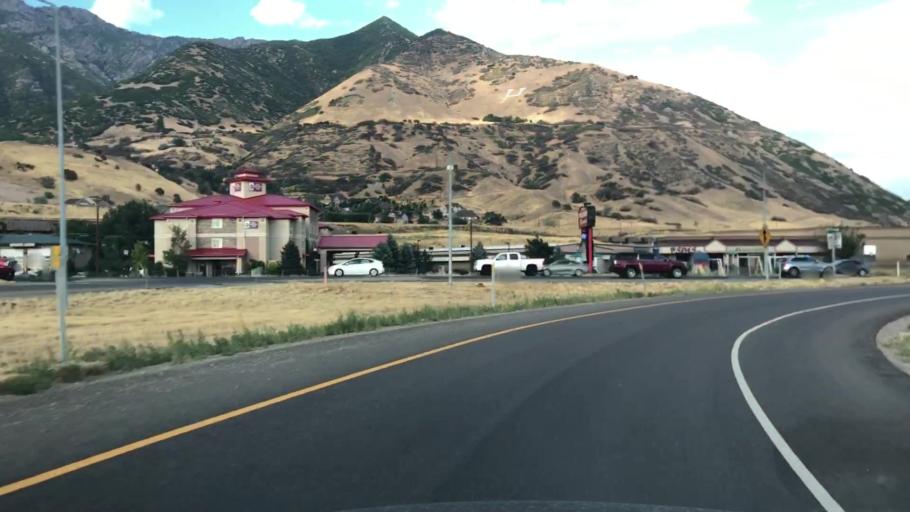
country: US
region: Utah
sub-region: Weber County
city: Uintah
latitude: 41.1386
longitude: -111.9125
